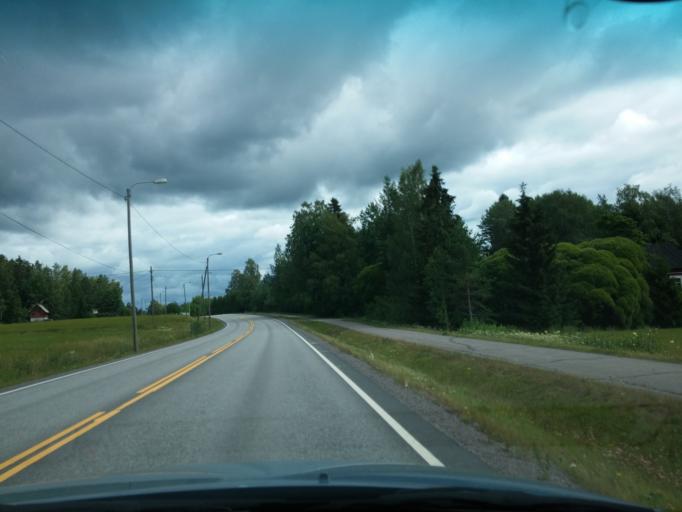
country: FI
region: Uusimaa
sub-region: Porvoo
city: Askola
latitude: 60.5122
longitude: 25.5761
